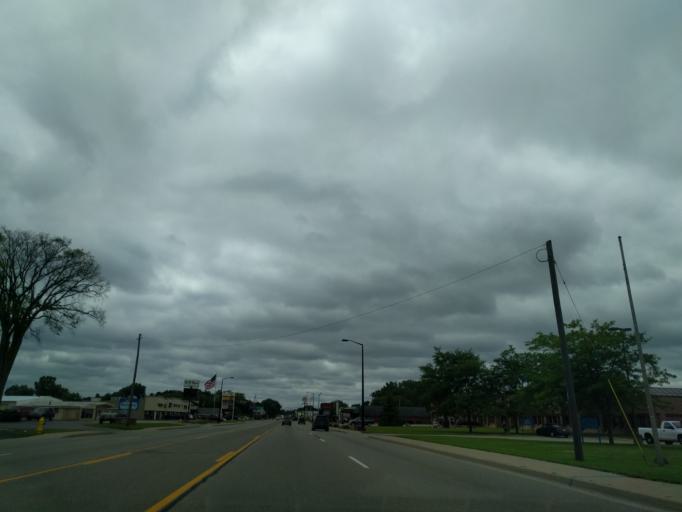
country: US
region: Michigan
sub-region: Menominee County
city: Menominee
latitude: 45.1219
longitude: -87.6134
